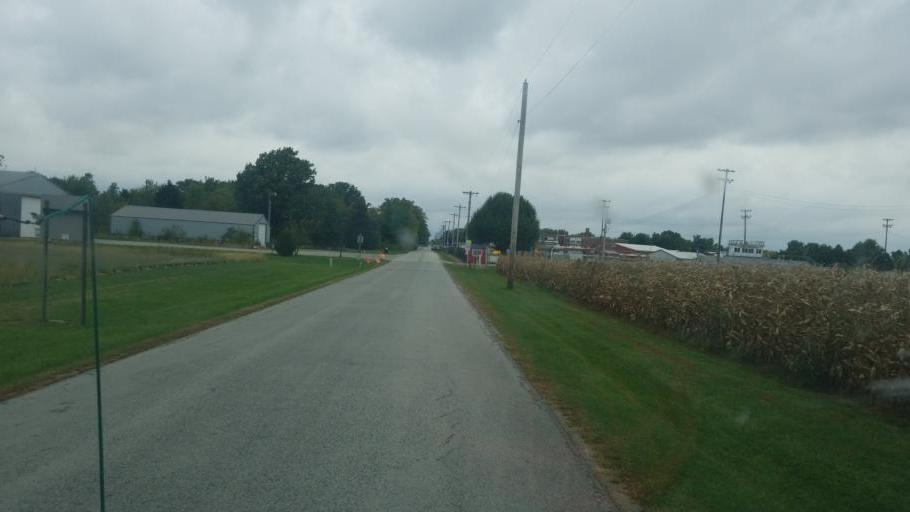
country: US
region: Ohio
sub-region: Seneca County
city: Fostoria
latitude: 41.1037
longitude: -83.5164
